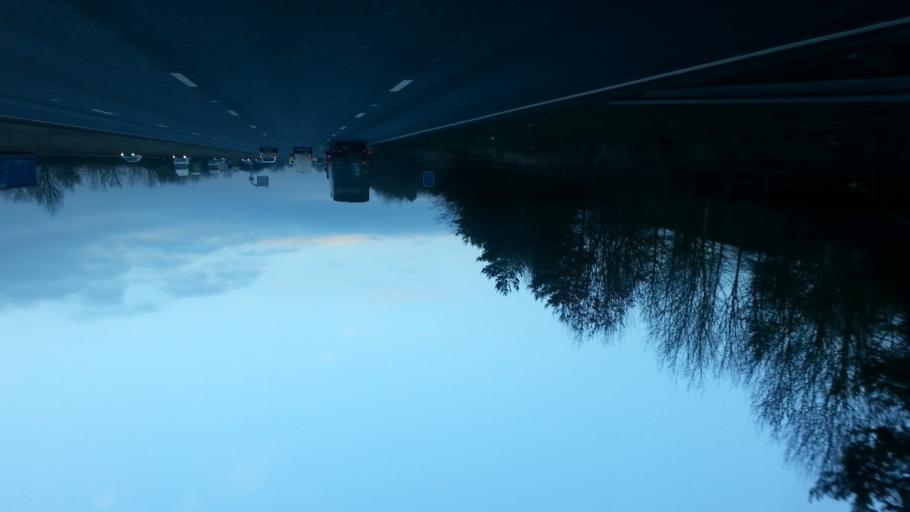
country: GB
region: England
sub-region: Worcestershire
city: Droitwich
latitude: 52.2401
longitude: -2.1351
